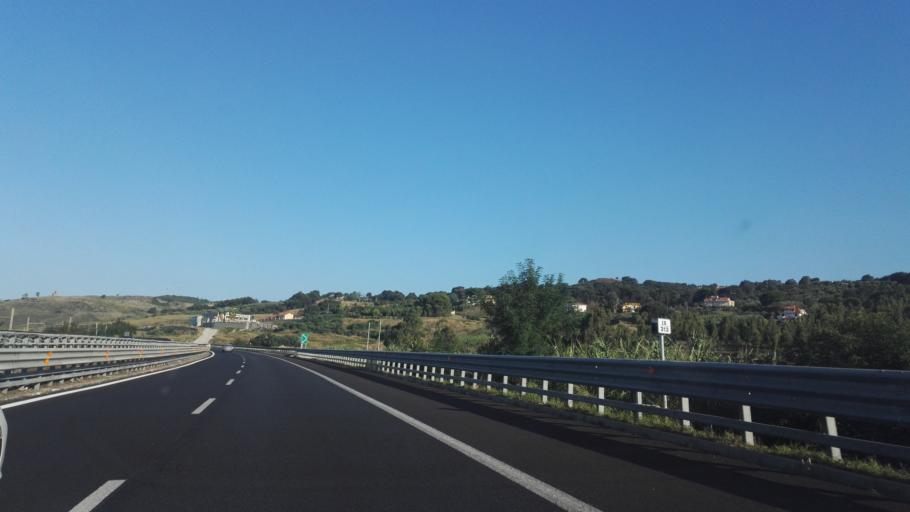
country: IT
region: Calabria
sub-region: Provincia di Catanzaro
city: Gizzeria
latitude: 38.9479
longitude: 16.1851
